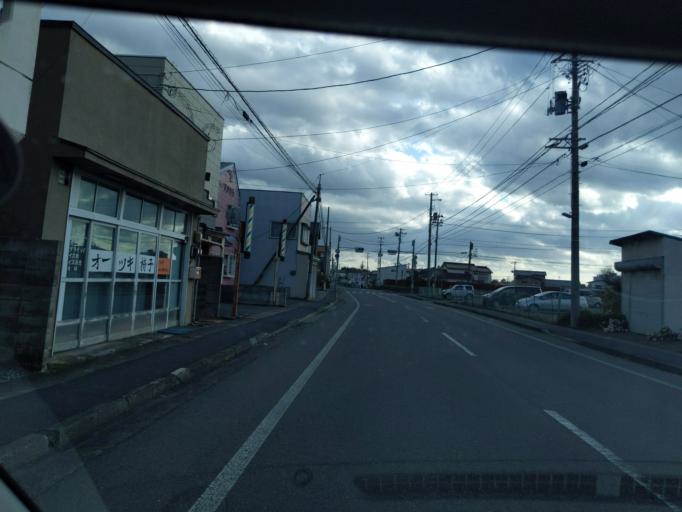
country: JP
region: Iwate
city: Mizusawa
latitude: 39.1330
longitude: 141.1412
